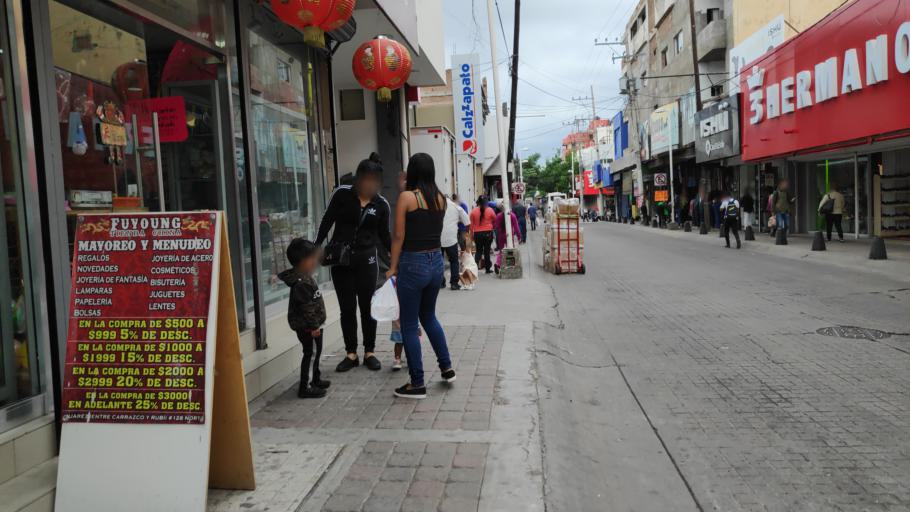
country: MX
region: Sinaloa
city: Culiacan
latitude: 24.8072
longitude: -107.3957
